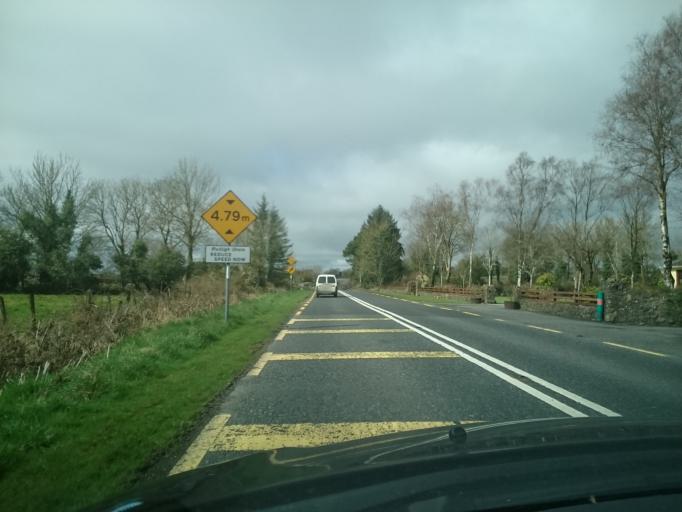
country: IE
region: Connaught
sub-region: Maigh Eo
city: Claremorris
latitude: 53.7201
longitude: -8.9372
